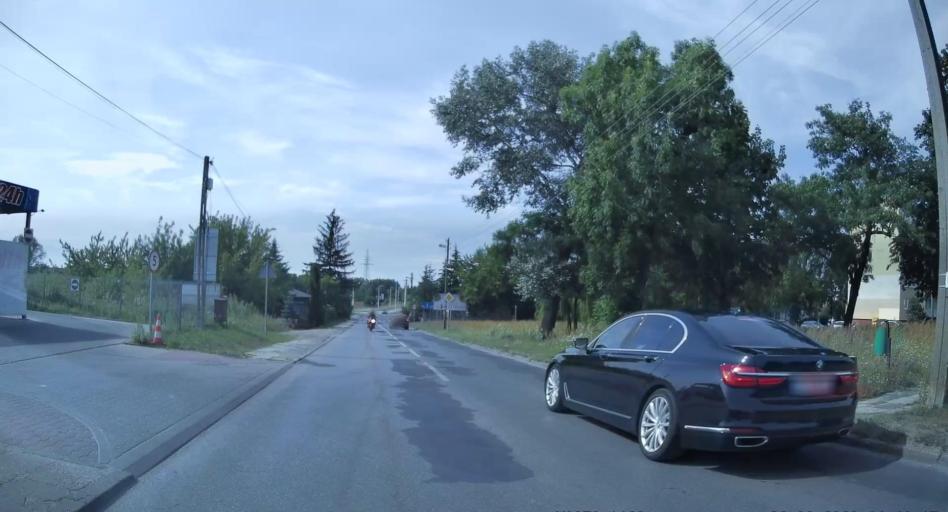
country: PL
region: Lodz Voivodeship
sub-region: Powiat tomaszowski
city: Tomaszow Mazowiecki
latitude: 51.5430
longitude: 19.9960
